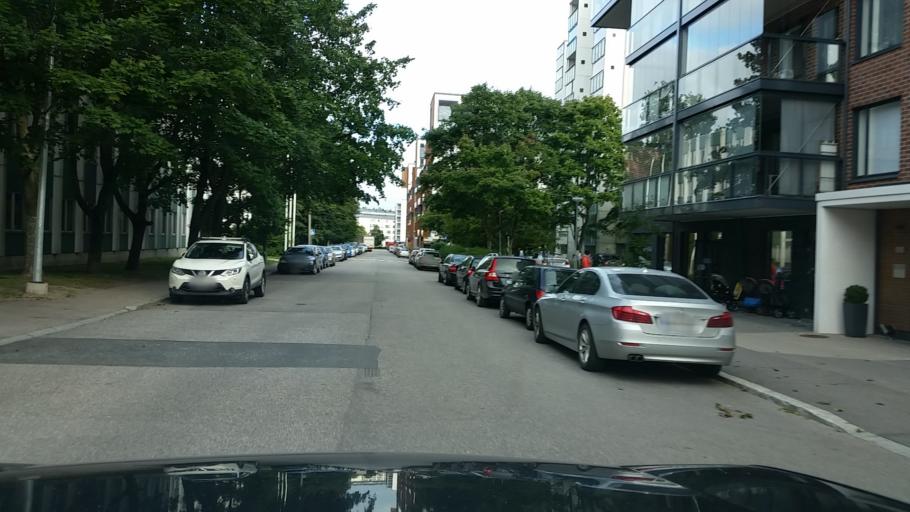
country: FI
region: Uusimaa
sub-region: Helsinki
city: Helsinki
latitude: 60.1512
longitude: 24.8827
